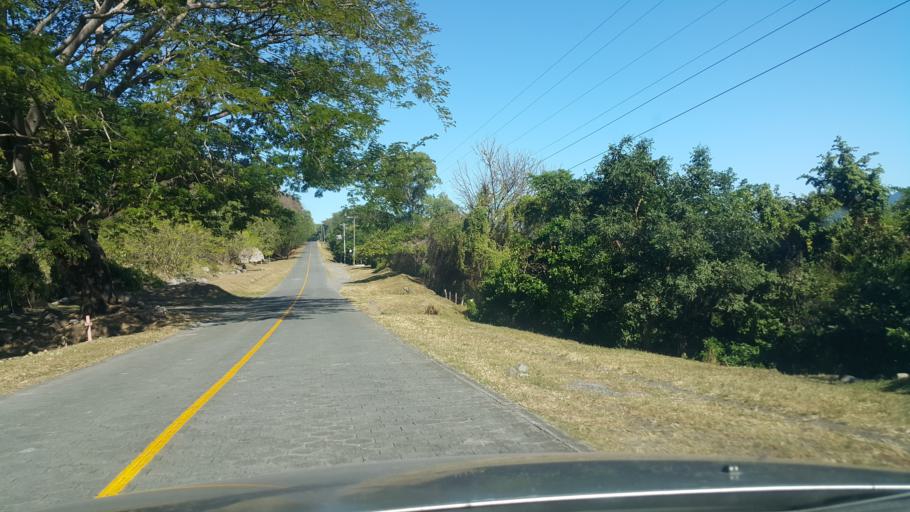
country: NI
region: Rivas
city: Altagracia
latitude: 11.4960
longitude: -85.6243
